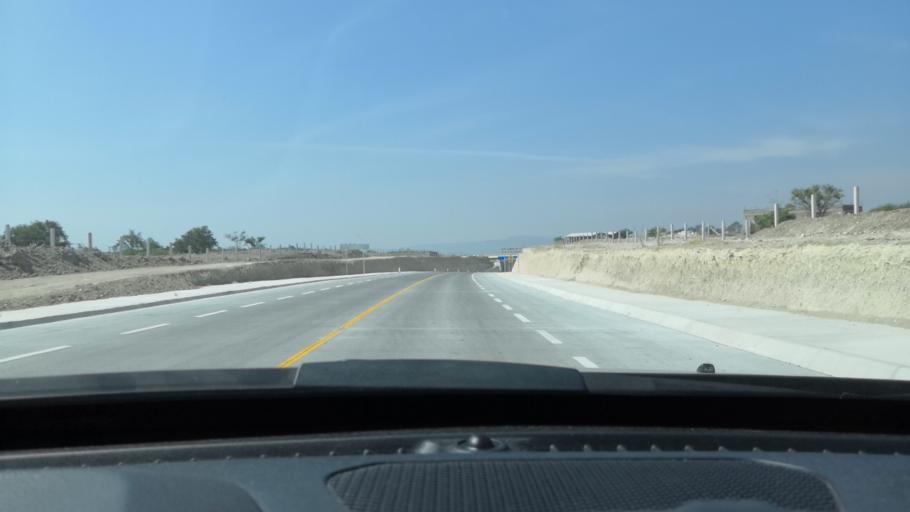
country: MX
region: Guanajuato
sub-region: Leon
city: Malagana (San Antonio del Monte)
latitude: 21.0907
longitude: -101.7929
